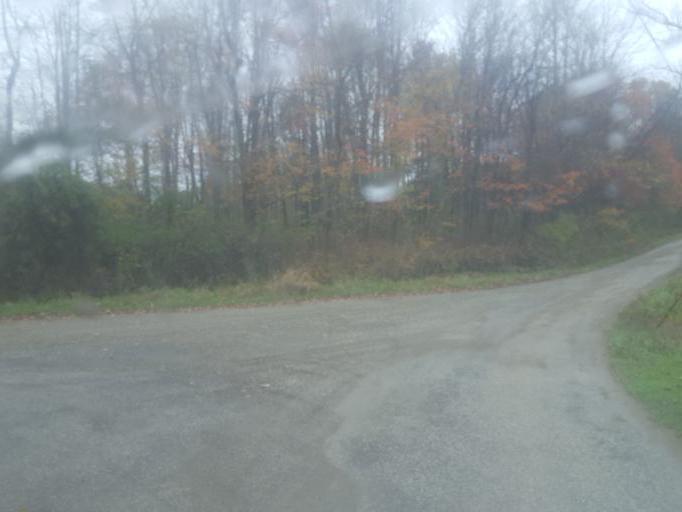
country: US
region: Ohio
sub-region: Holmes County
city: Millersburg
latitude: 40.5149
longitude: -81.9492
